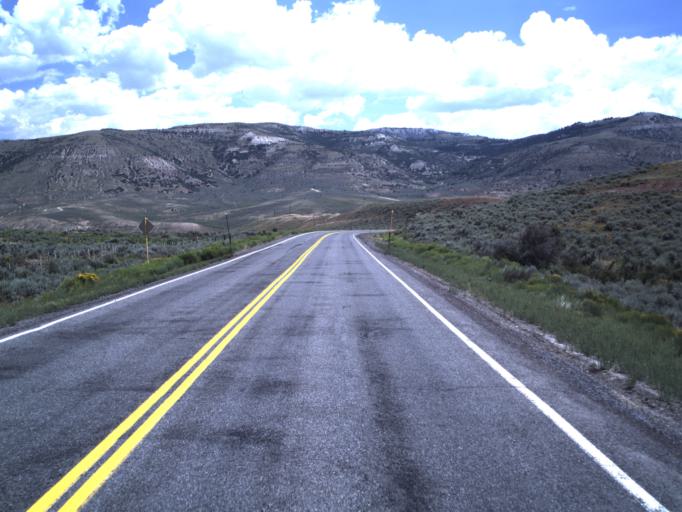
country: US
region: Utah
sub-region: Carbon County
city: Helper
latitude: 39.8588
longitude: -111.0491
